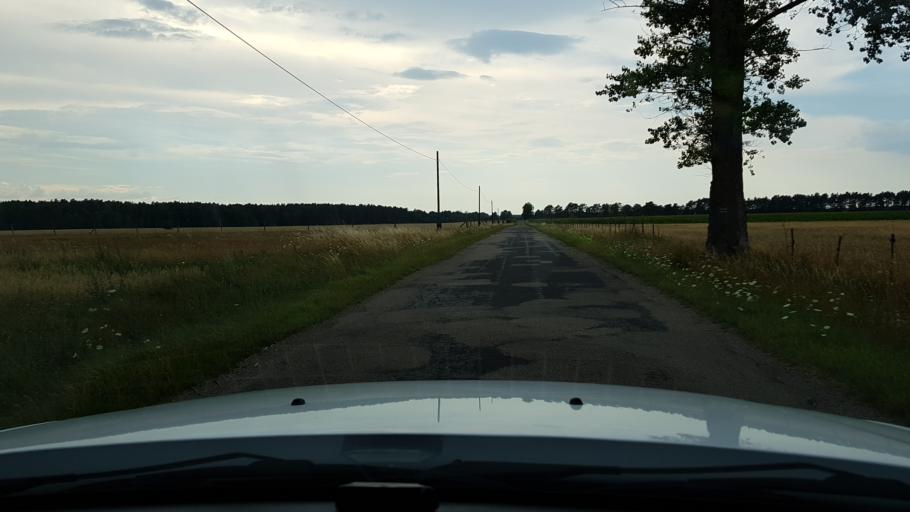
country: PL
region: West Pomeranian Voivodeship
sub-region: Powiat drawski
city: Czaplinek
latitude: 53.4319
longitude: 16.2993
